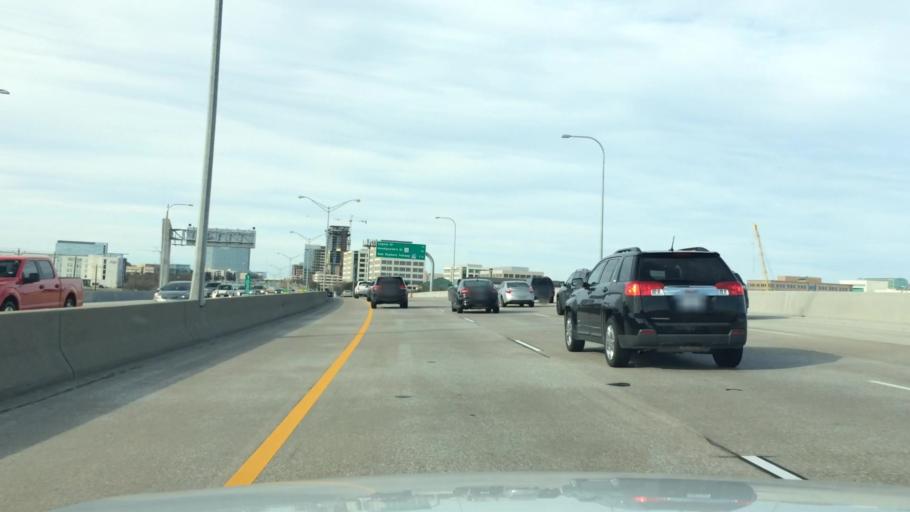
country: US
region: Texas
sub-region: Denton County
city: The Colony
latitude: 33.0653
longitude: -96.8247
